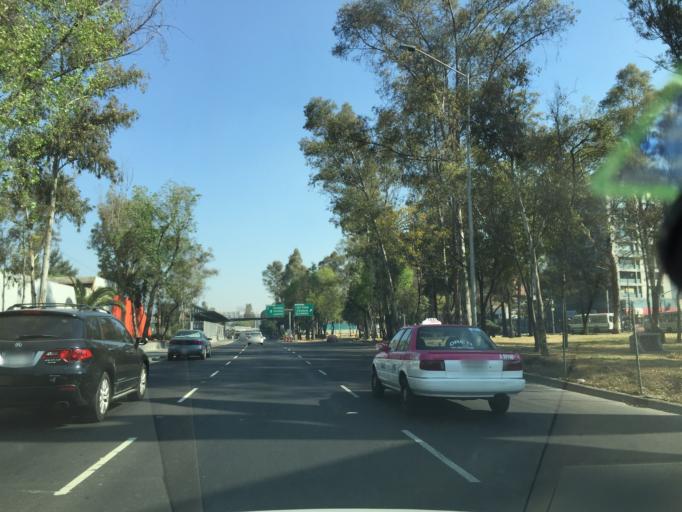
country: MX
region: Mexico
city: Colonia Lindavista
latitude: 19.4851
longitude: -99.1253
